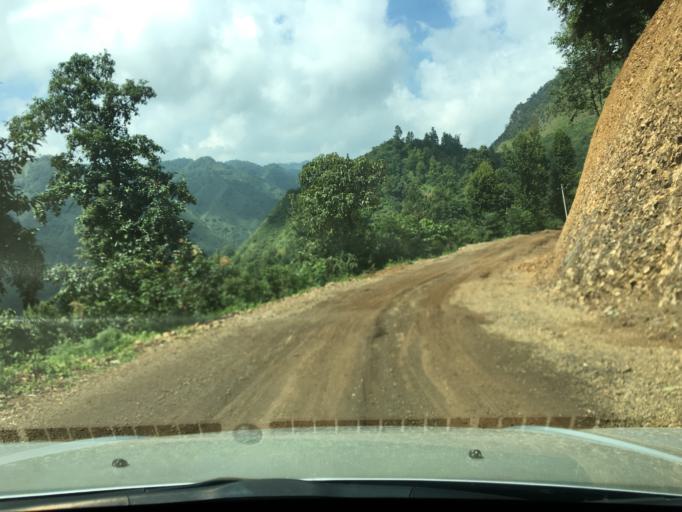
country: CN
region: Guizhou Sheng
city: Liupanshui
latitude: 25.9090
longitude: 105.1024
